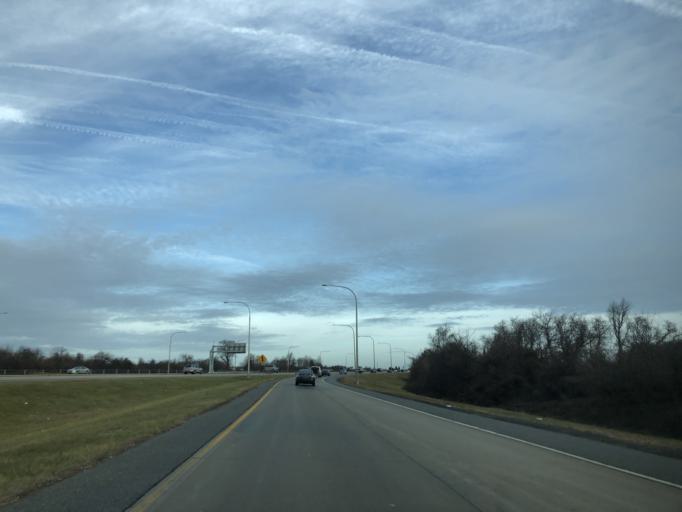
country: US
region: Delaware
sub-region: New Castle County
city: Bear
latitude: 39.5821
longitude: -75.6612
